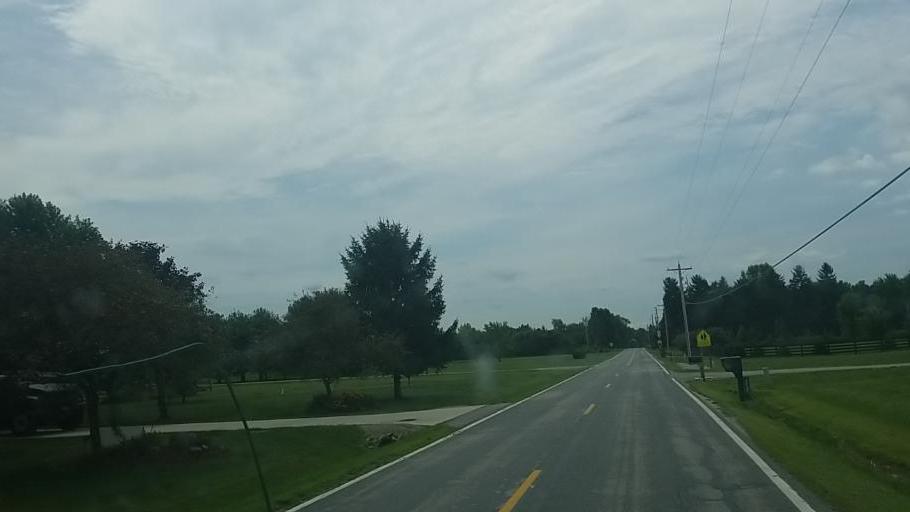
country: US
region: Ohio
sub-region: Delaware County
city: Sunbury
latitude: 40.1722
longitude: -82.8267
